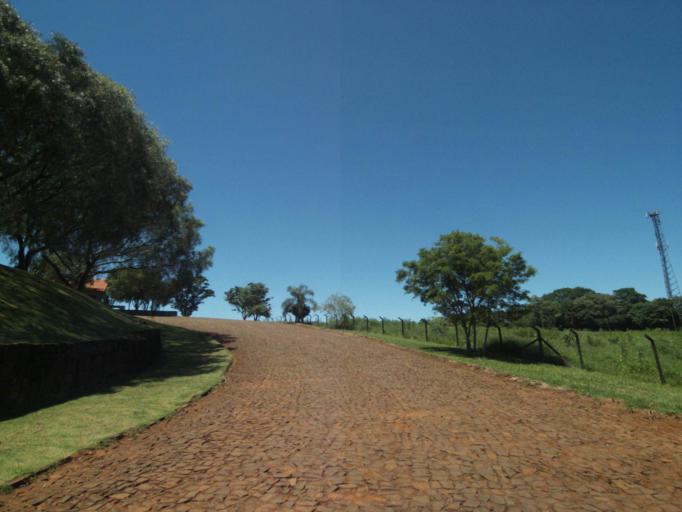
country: BR
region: Parana
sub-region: Pato Branco
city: Pato Branco
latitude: -26.2603
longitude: -52.7731
